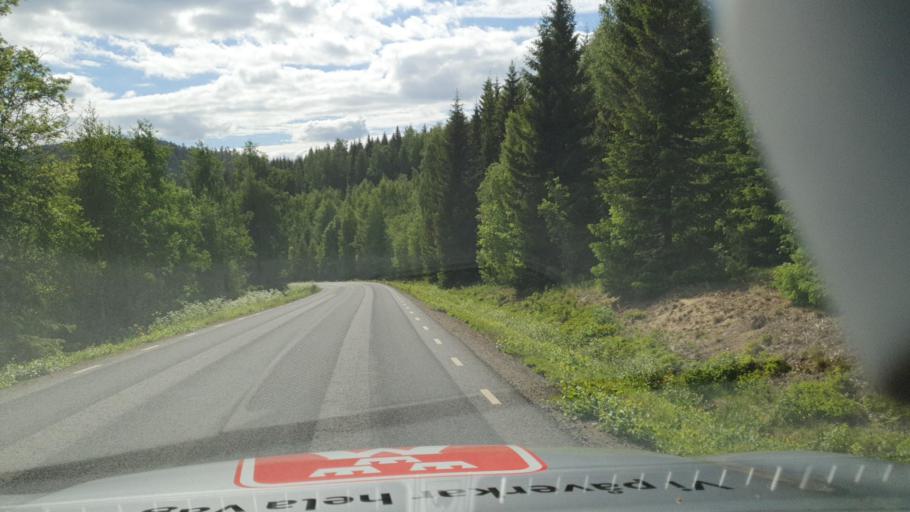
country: SE
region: Vaesternorrland
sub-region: Kramfors Kommun
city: Nordingra
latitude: 62.8316
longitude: 18.1847
